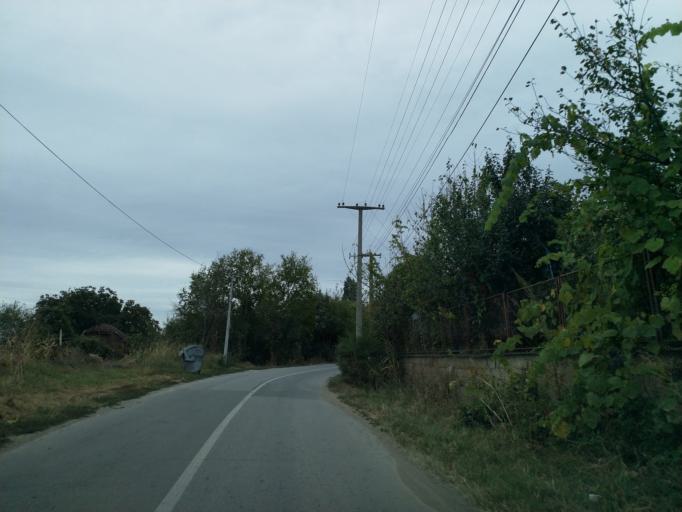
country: RS
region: Central Serbia
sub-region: Pomoravski Okrug
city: Cuprija
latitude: 43.8768
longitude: 21.3192
